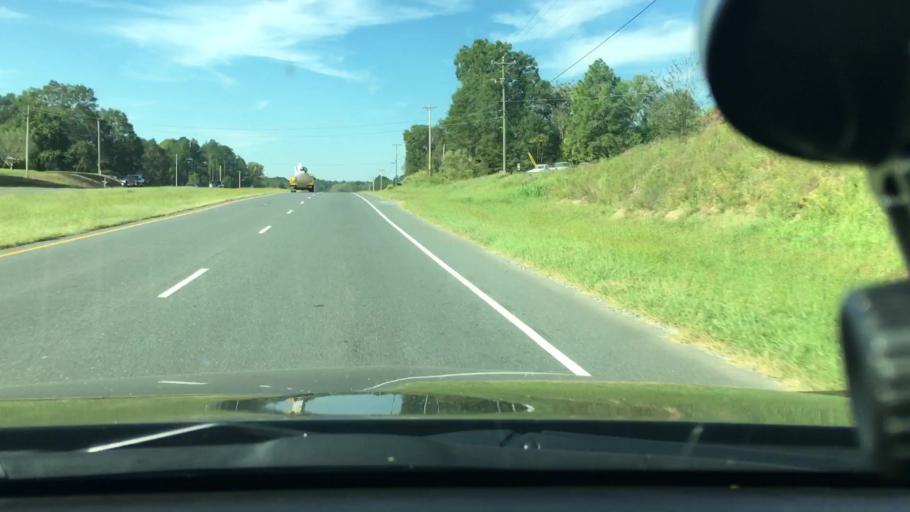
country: US
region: North Carolina
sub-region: Stanly County
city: Albemarle
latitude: 35.3081
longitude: -80.2686
